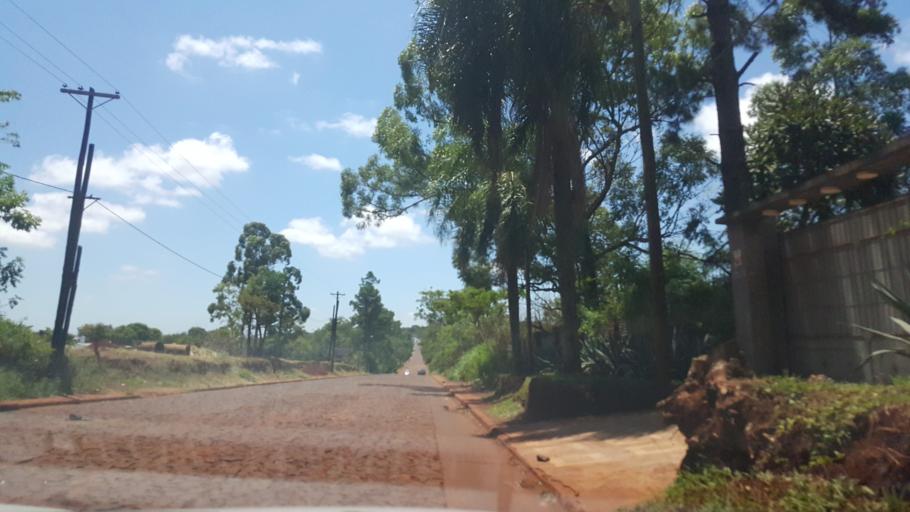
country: AR
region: Misiones
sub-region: Departamento de Capital
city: Posadas
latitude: -27.4059
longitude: -55.9449
